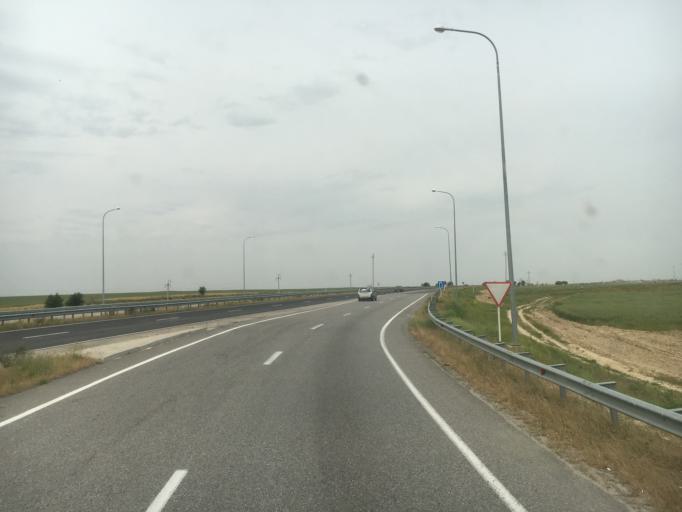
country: KZ
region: Ongtustik Qazaqstan
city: Temirlanovka
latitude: 42.5303
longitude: 69.3422
